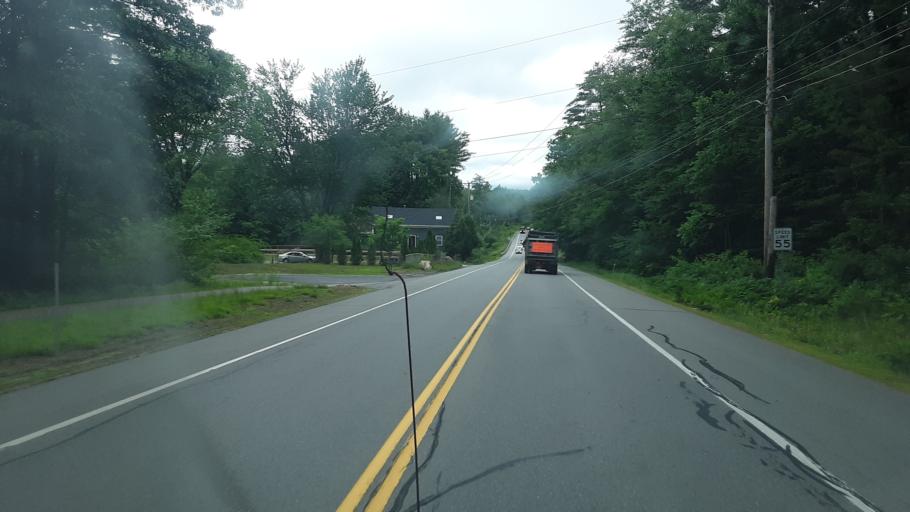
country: US
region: New Hampshire
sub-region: Rockingham County
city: Nottingham
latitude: 43.1567
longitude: -71.0665
